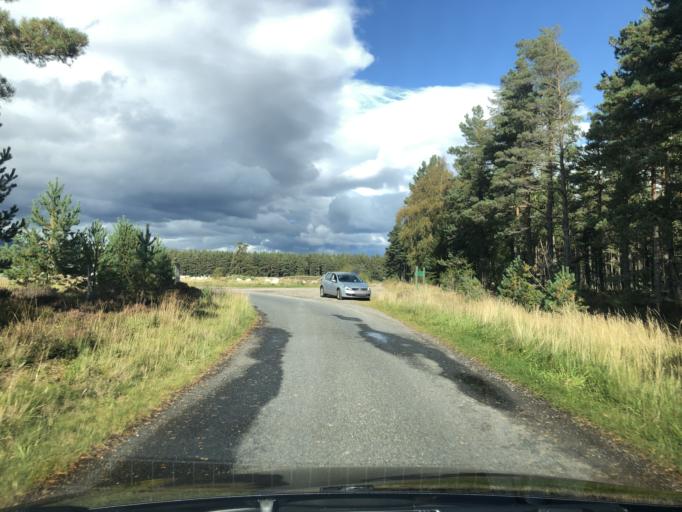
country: GB
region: Scotland
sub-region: Highland
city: Aviemore
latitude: 57.1054
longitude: -3.8873
